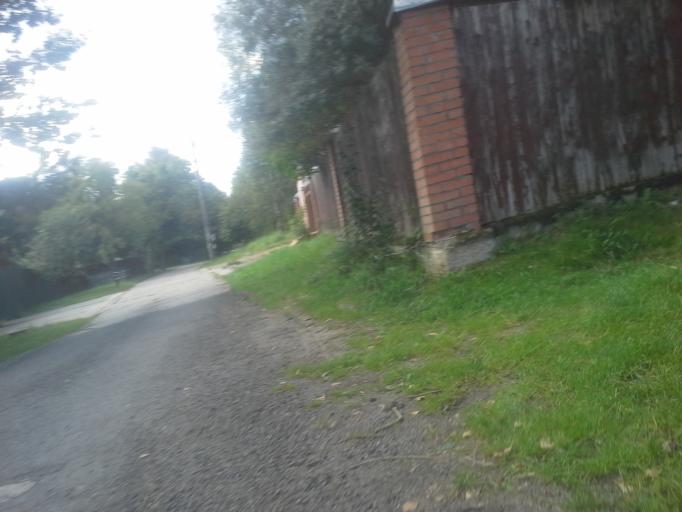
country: RU
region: Moskovskaya
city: Selyatino
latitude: 55.4883
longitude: 36.9977
